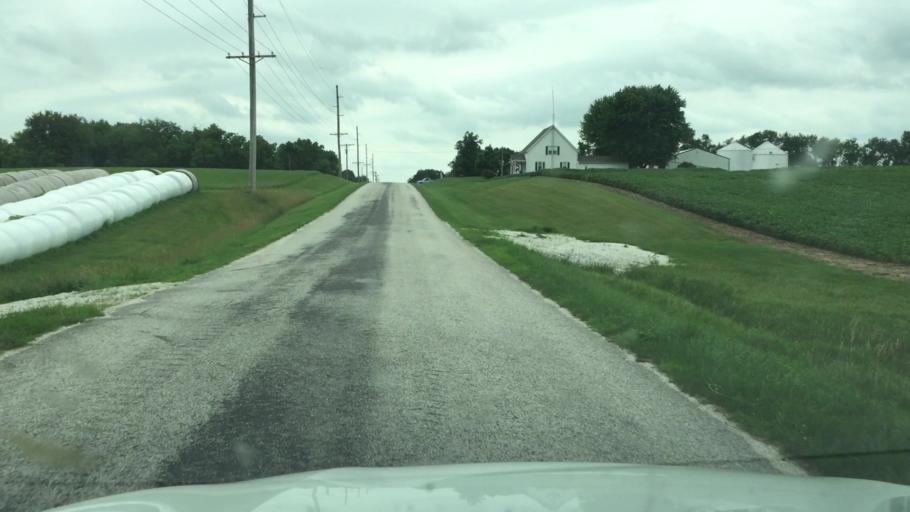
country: US
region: Illinois
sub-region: Hancock County
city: Carthage
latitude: 40.2996
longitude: -91.0831
